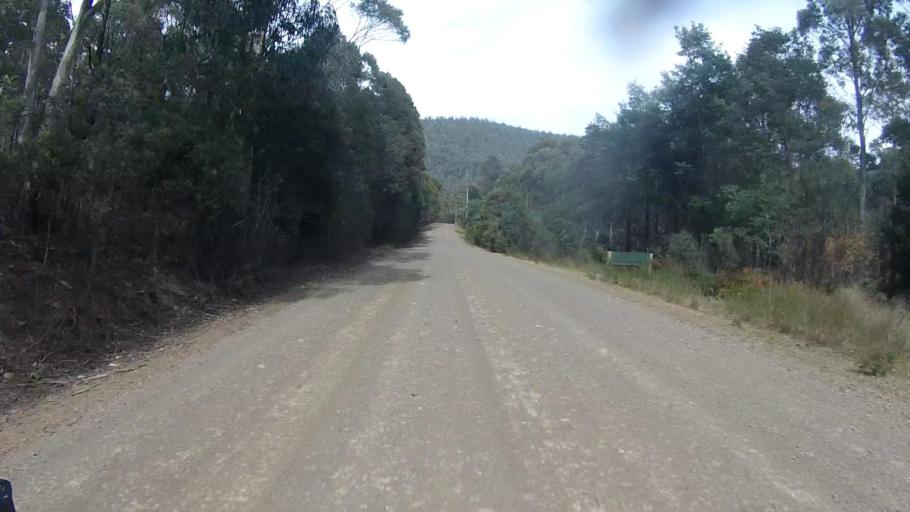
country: AU
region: Tasmania
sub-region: Sorell
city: Sorell
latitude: -42.6887
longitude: 147.8697
